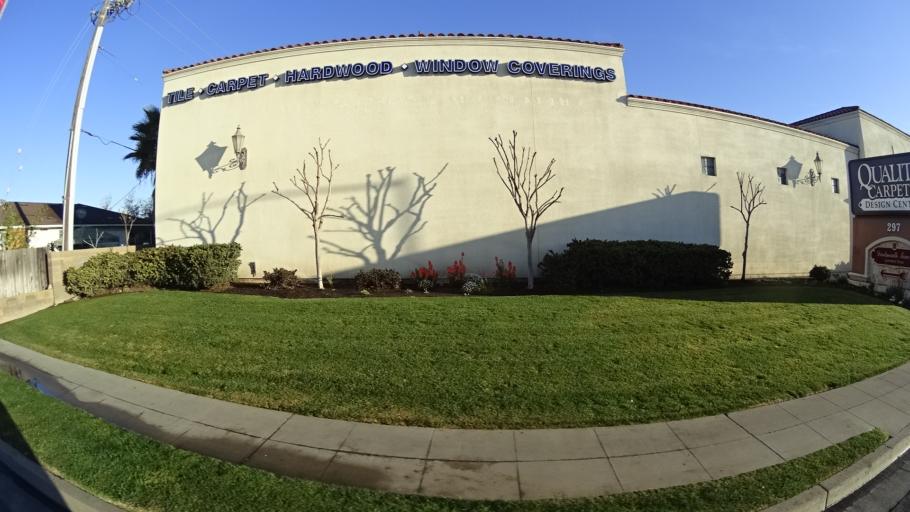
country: US
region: California
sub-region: Fresno County
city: Tarpey Village
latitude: 36.8086
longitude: -119.7055
